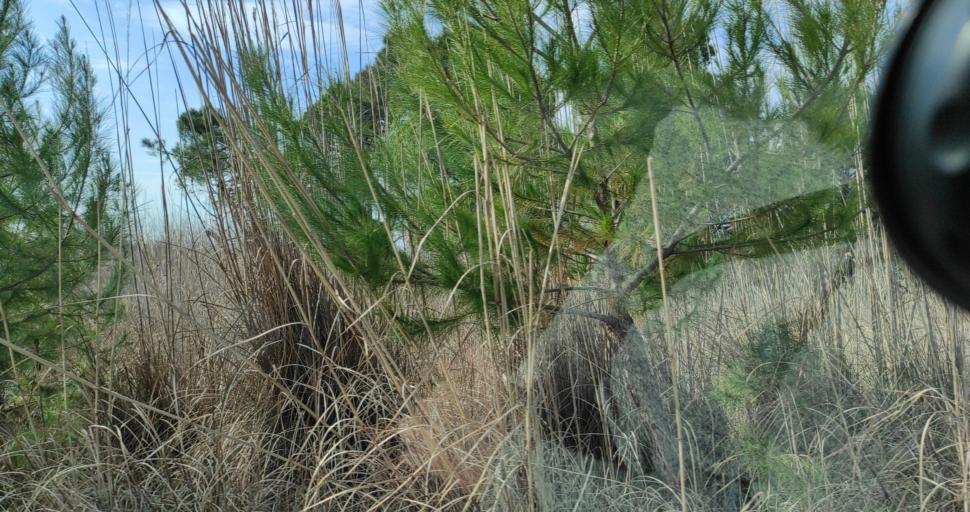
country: AL
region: Lezhe
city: Shengjin
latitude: 41.7651
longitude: 19.5966
